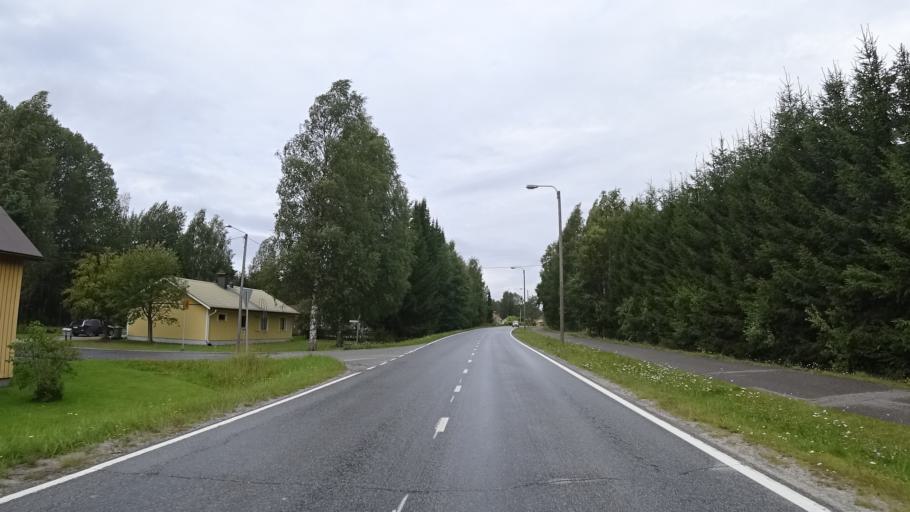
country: FI
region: Southern Savonia
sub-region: Savonlinna
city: Kerimaeki
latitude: 61.9225
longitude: 29.2800
